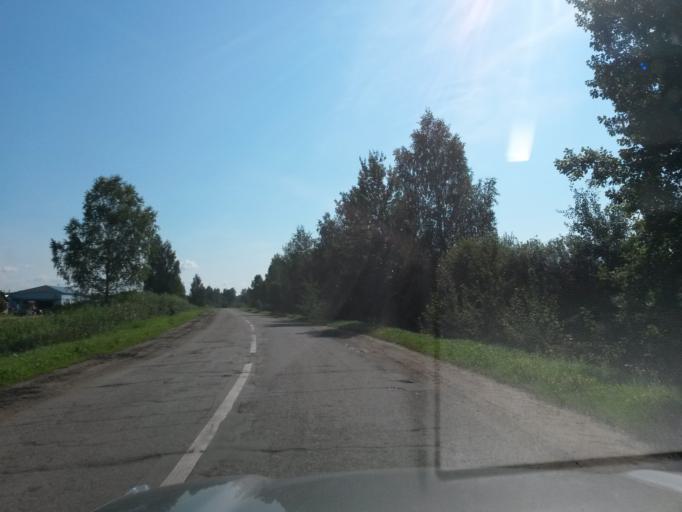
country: RU
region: Jaroslavl
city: Gavrilov-Yam
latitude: 57.3028
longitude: 39.9916
